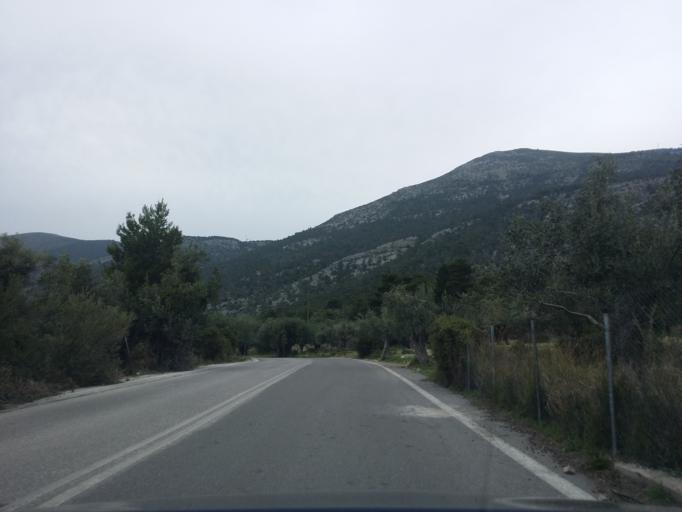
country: GR
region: Central Greece
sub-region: Nomos Voiotias
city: Kaparellion
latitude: 38.1544
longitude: 23.2339
